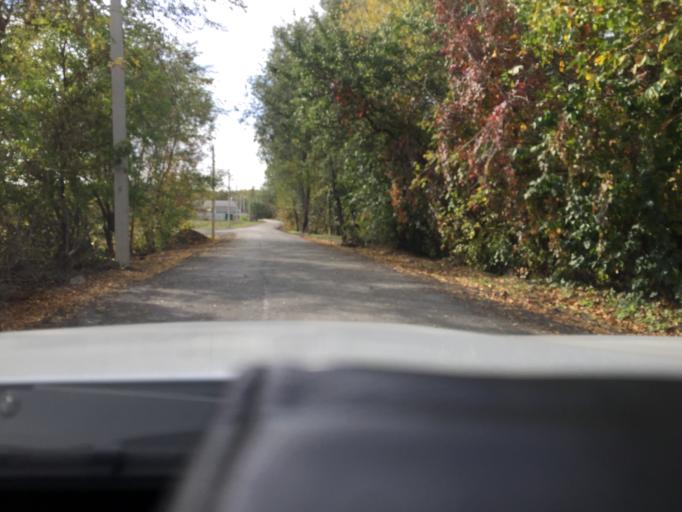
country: RU
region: Rostov
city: Aksay
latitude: 47.3035
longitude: 39.8316
